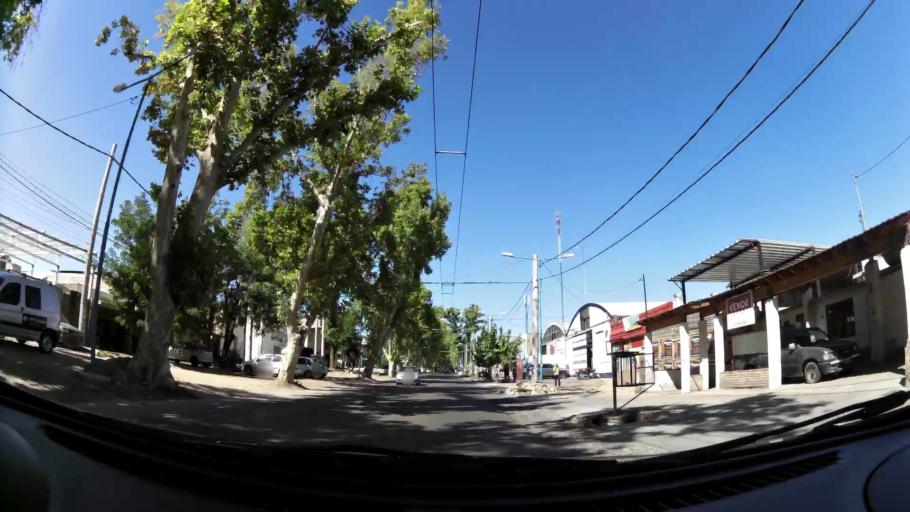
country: AR
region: Mendoza
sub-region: Departamento de Godoy Cruz
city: Godoy Cruz
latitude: -32.9402
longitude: -68.8414
